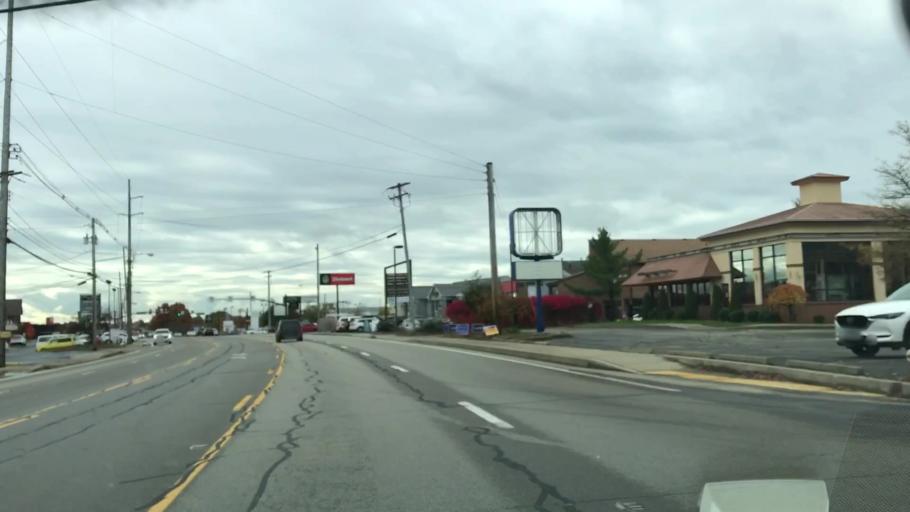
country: US
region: Pennsylvania
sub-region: Allegheny County
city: Bradford Woods
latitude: 40.6179
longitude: -80.0557
